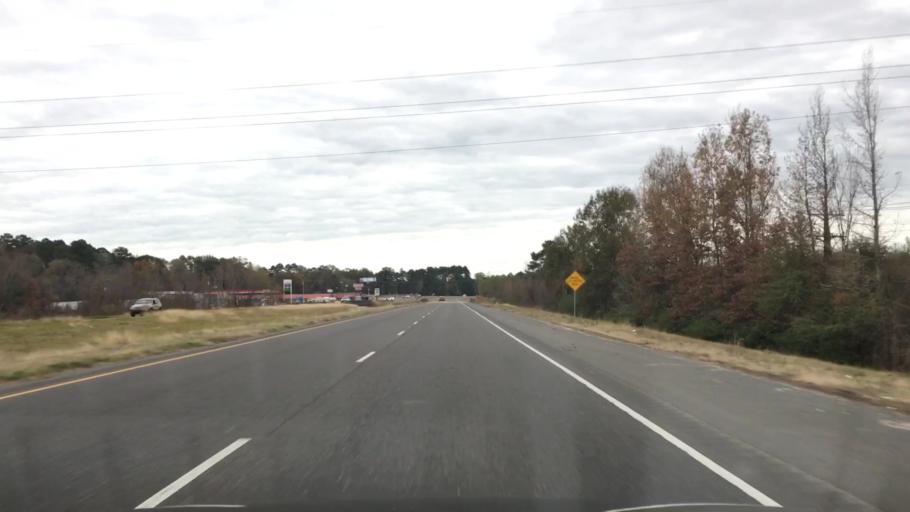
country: US
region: Louisiana
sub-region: Vernon Parish
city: New Llano
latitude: 31.1056
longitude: -93.2705
